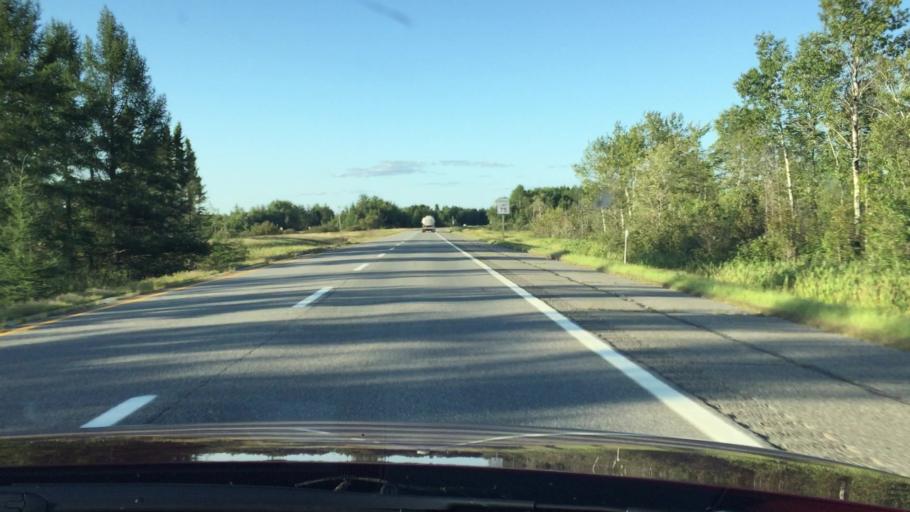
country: US
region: Maine
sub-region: Penobscot County
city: Patten
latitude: 45.8815
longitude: -68.4083
